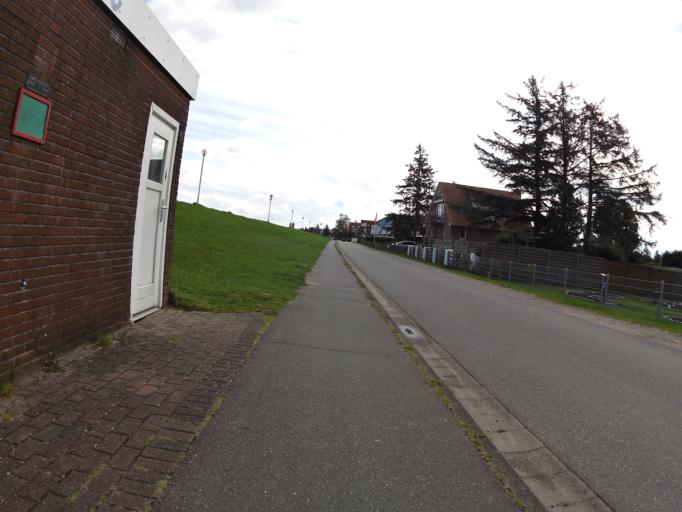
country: DE
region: Schleswig-Holstein
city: Wisch
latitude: 54.4295
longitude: 10.3623
